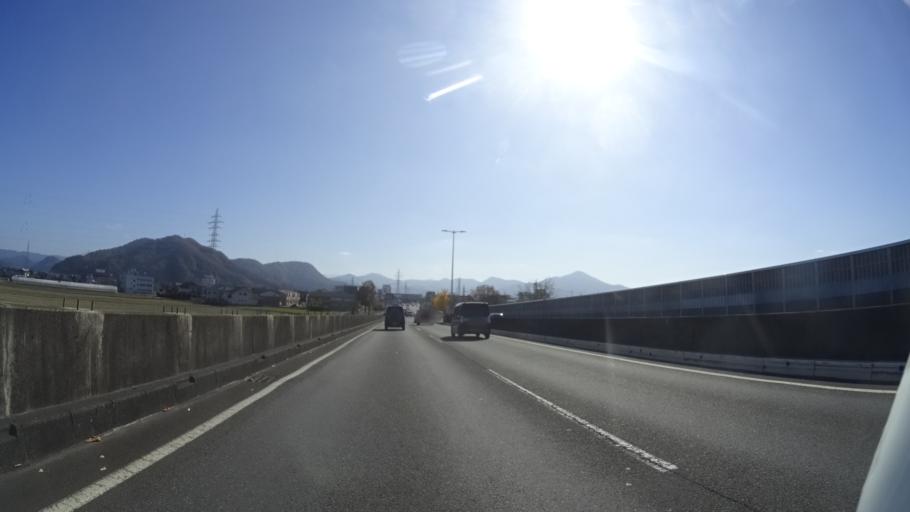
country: JP
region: Fukui
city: Sabae
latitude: 35.9523
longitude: 136.1912
